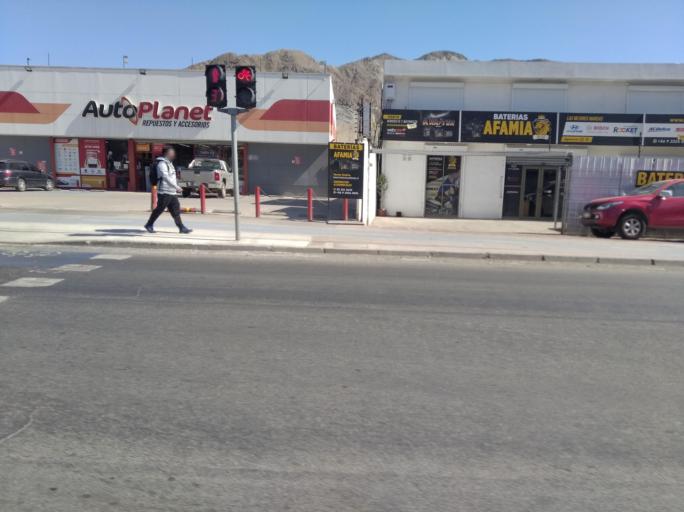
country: CL
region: Atacama
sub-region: Provincia de Copiapo
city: Copiapo
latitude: -27.3644
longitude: -70.3431
